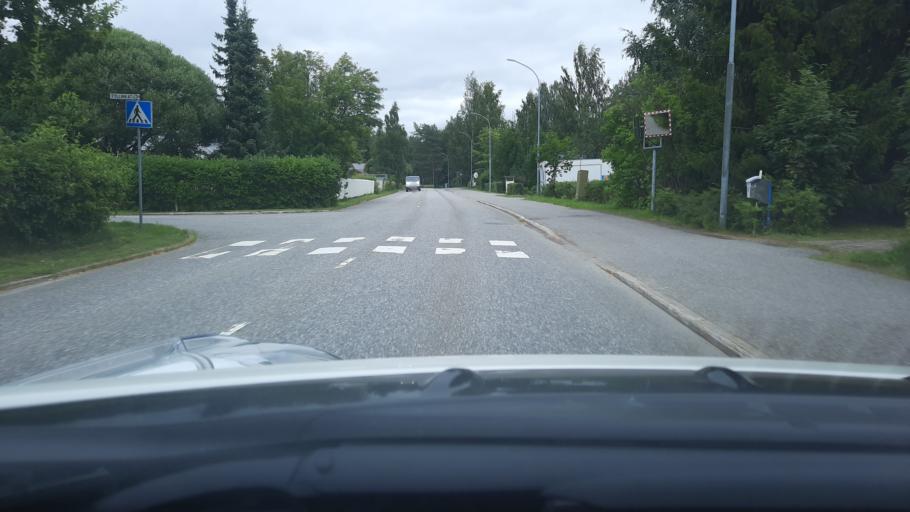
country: FI
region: North Karelia
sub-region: Joensuu
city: Joensuu
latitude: 62.6103
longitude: 29.8051
